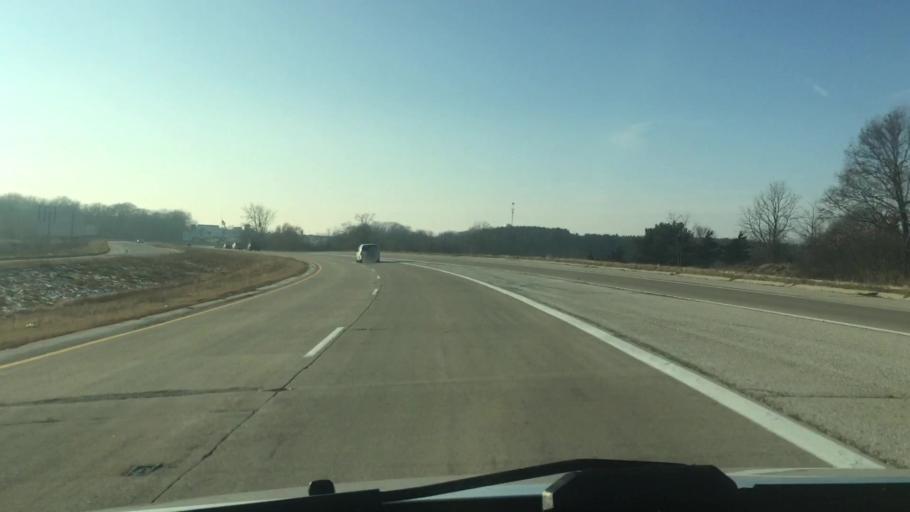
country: US
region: Wisconsin
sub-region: Waukesha County
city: Okauchee Lake
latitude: 43.1083
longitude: -88.4656
